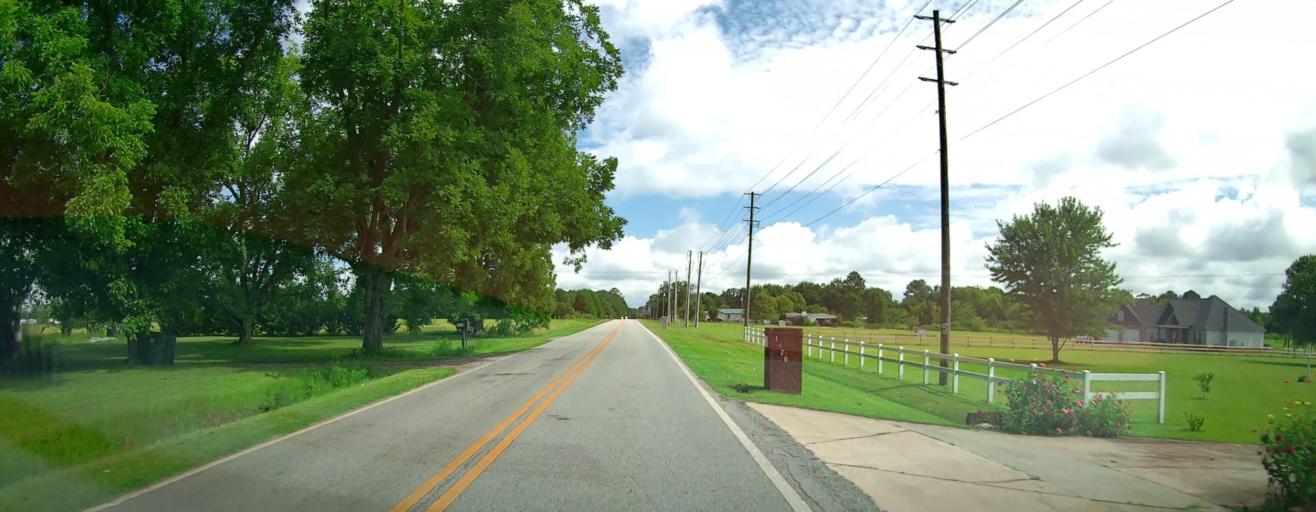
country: US
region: Georgia
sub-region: Peach County
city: Byron
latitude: 32.6256
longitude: -83.7995
